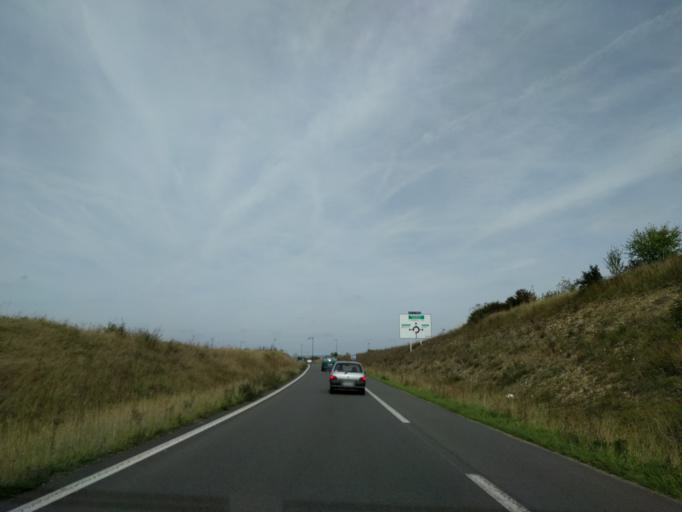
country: FR
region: Centre
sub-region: Departement du Cher
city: Bourges
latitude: 47.0816
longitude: 2.4429
